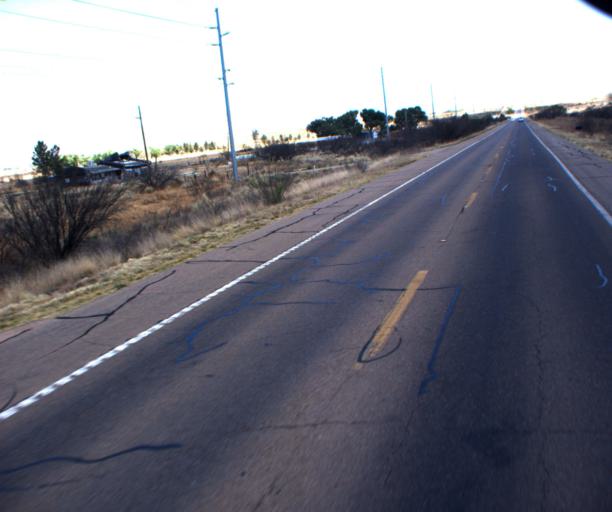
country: US
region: Arizona
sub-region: Cochise County
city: Sierra Vista Southeast
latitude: 31.3800
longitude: -110.1095
